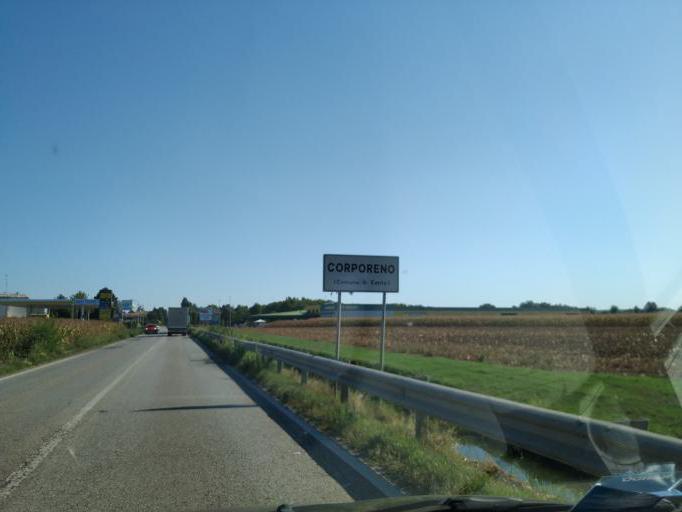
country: IT
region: Emilia-Romagna
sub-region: Provincia di Ferrara
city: Corpo Reno
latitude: 44.7508
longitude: 11.3015
